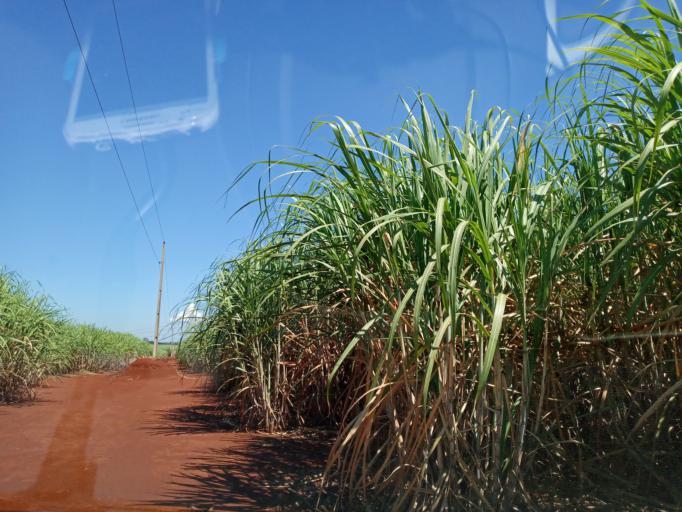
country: BR
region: Goias
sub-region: Itumbiara
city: Itumbiara
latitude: -18.4418
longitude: -49.1344
